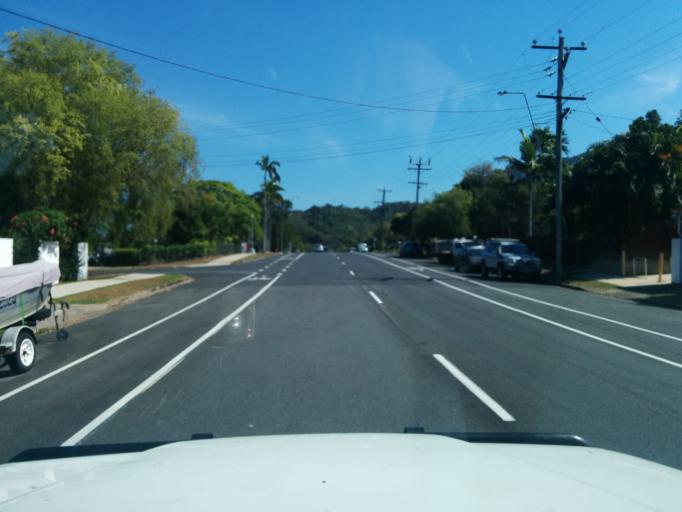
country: AU
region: Queensland
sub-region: Cairns
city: Redlynch
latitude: -16.9071
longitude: 145.7285
